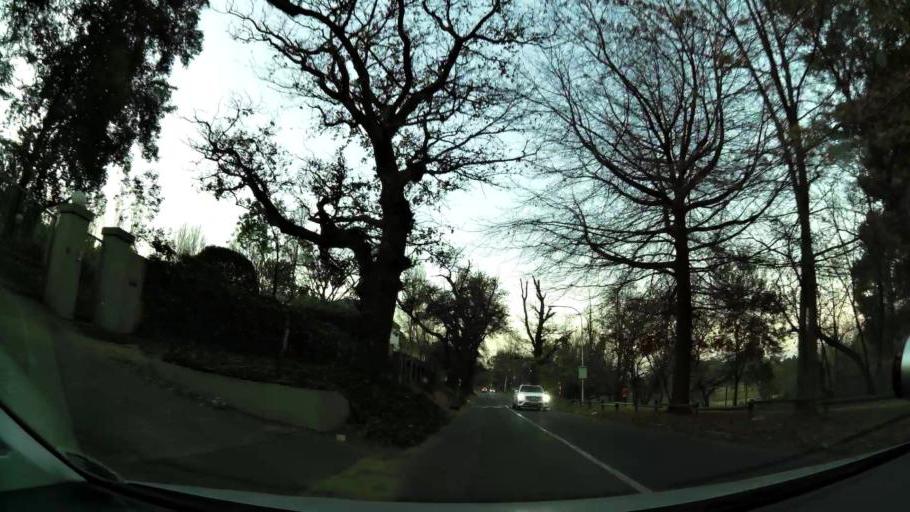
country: ZA
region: Gauteng
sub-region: City of Johannesburg Metropolitan Municipality
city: Johannesburg
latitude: -26.1434
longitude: 28.0576
